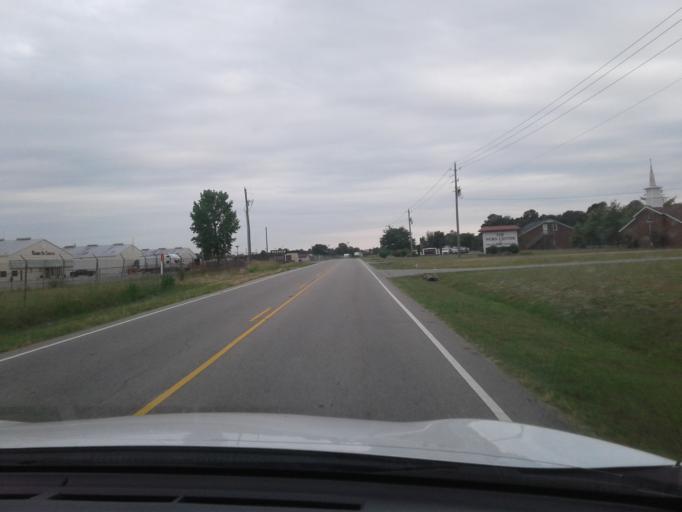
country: US
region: North Carolina
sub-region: Harnett County
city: Dunn
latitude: 35.3317
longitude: -78.5935
